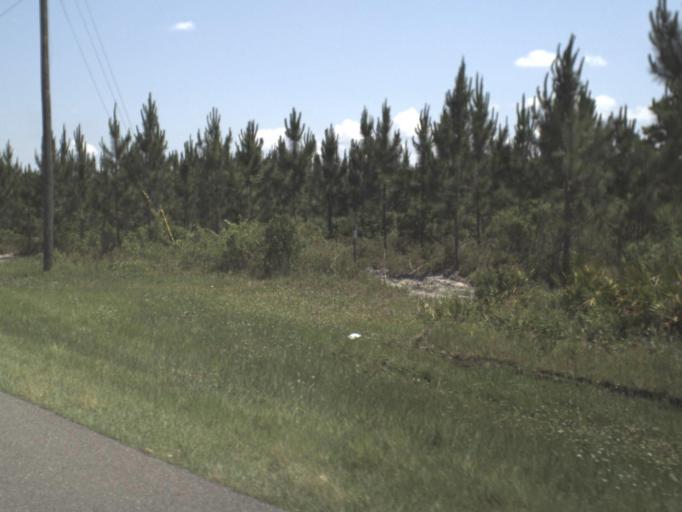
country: US
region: Florida
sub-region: Bradford County
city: Starke
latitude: 29.8752
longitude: -82.0789
